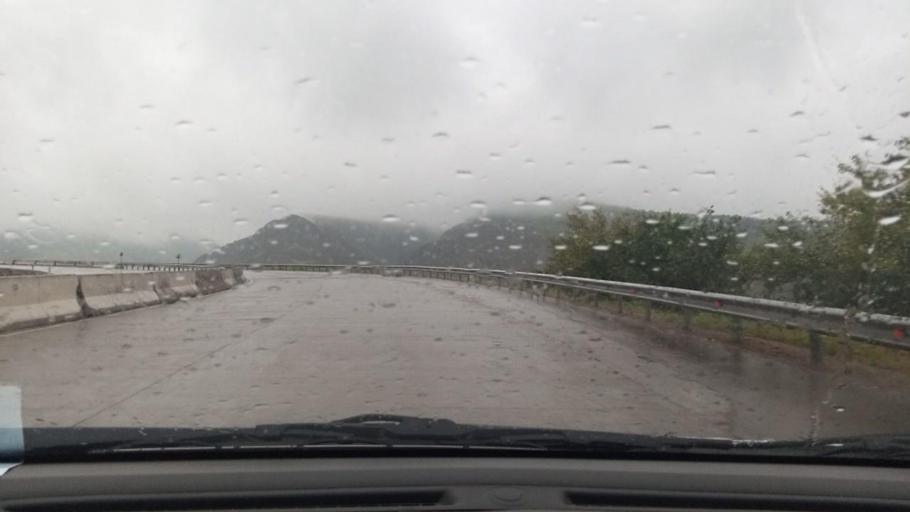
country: UZ
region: Toshkent
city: Angren
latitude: 41.0738
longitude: 70.2548
